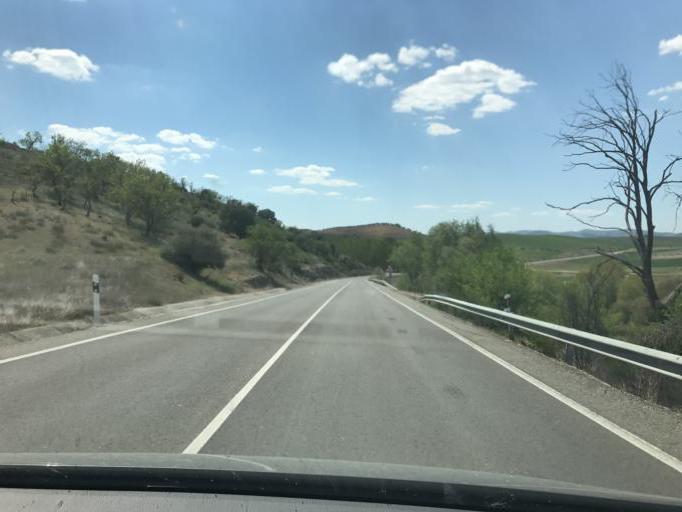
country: ES
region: Andalusia
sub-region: Provincia de Jaen
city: Frailes
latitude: 37.4401
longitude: -3.8404
